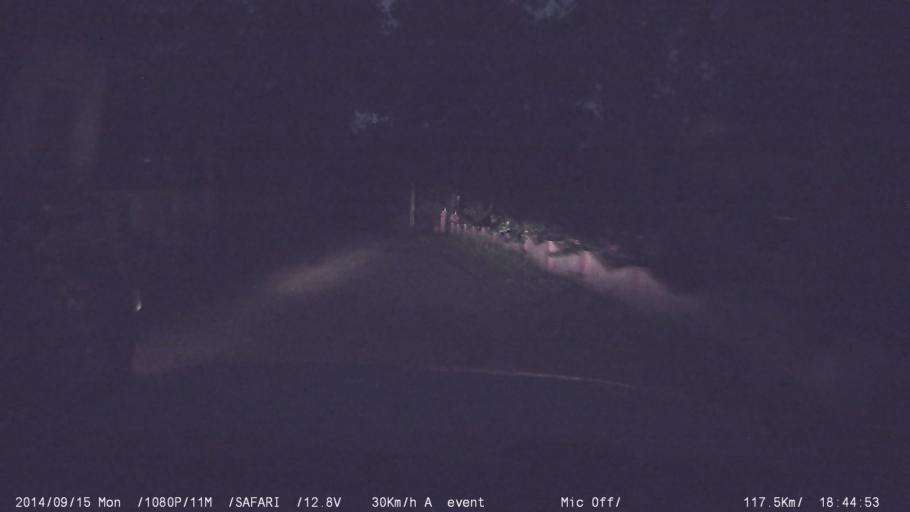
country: IN
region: Kerala
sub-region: Kottayam
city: Palackattumala
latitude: 9.7686
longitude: 76.5626
